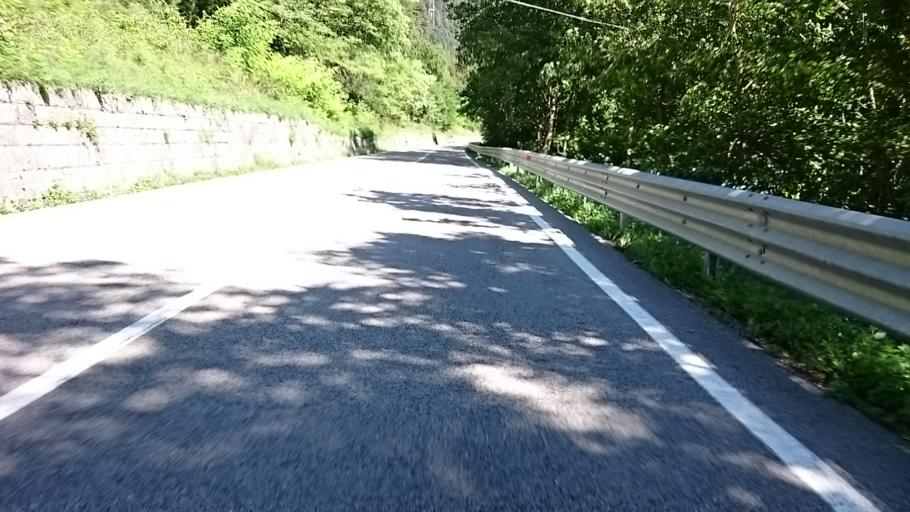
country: IT
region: Veneto
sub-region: Provincia di Belluno
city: Perarolo di Cadore
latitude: 46.4000
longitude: 12.3616
